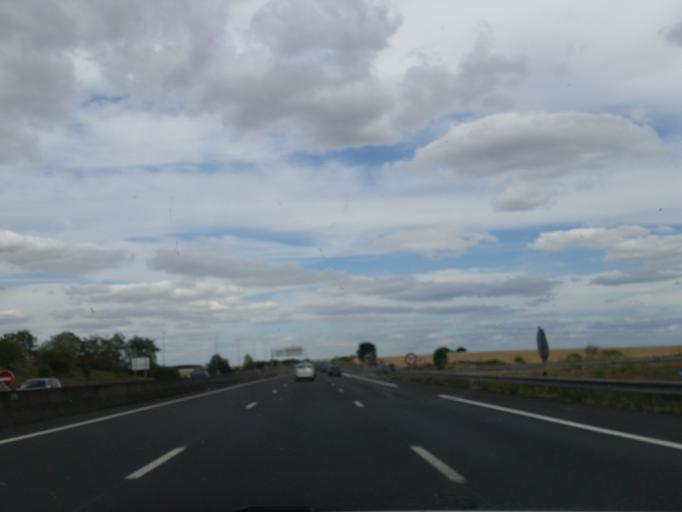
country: FR
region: Centre
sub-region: Departement d'Indre-et-Loire
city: Auzouer-en-Touraine
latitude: 47.5458
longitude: 0.9854
